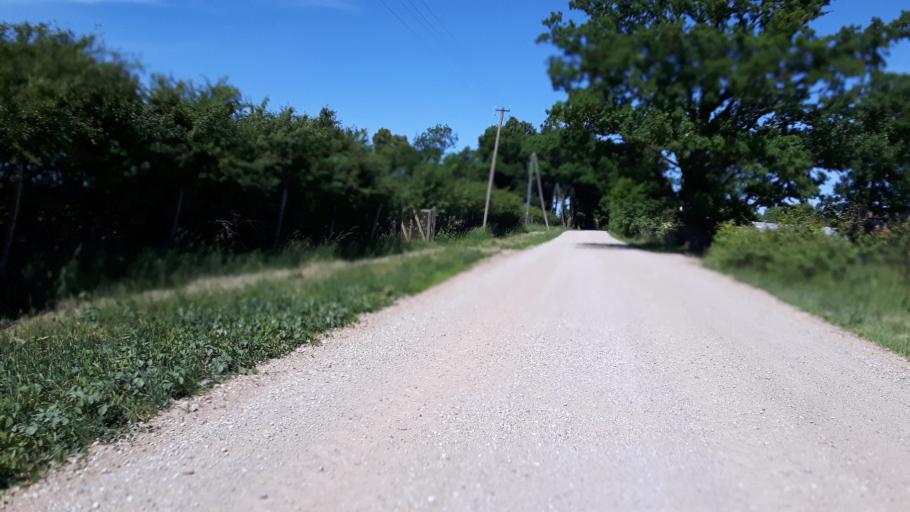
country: LV
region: Kandava
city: Kandava
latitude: 57.0426
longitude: 22.8791
